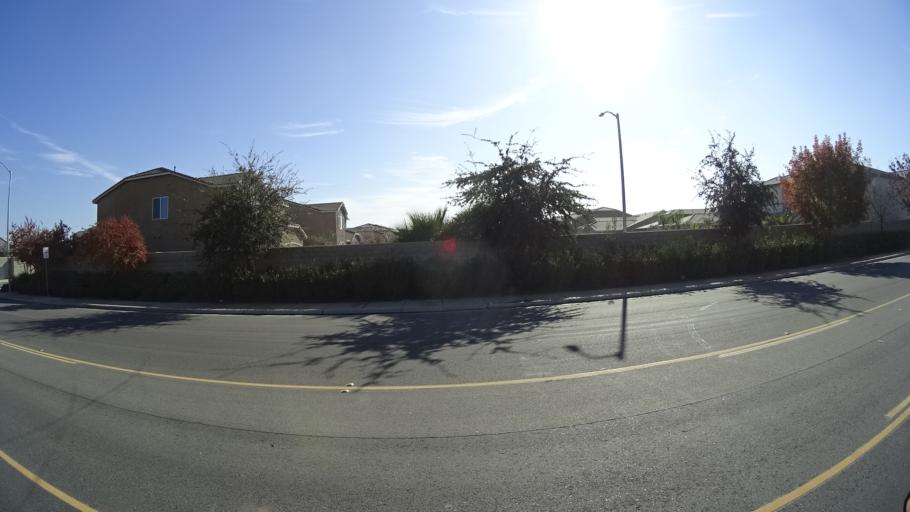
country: US
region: California
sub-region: Kern County
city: Greenfield
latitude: 35.2888
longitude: -119.0597
